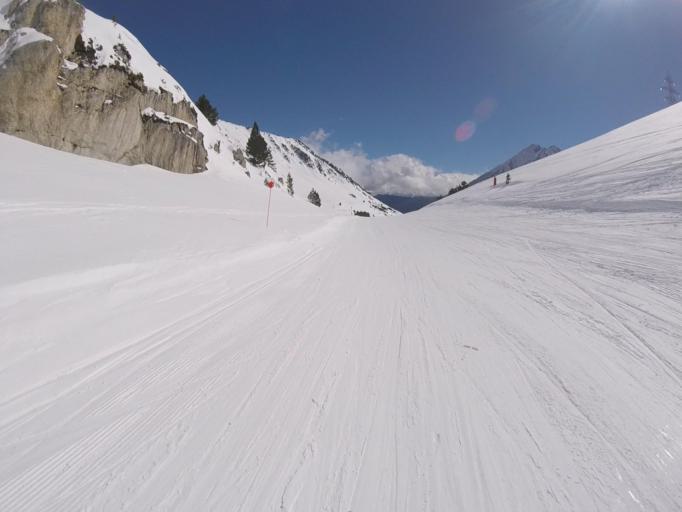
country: ES
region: Catalonia
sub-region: Provincia de Lleida
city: Espot
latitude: 42.6590
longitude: 0.9907
